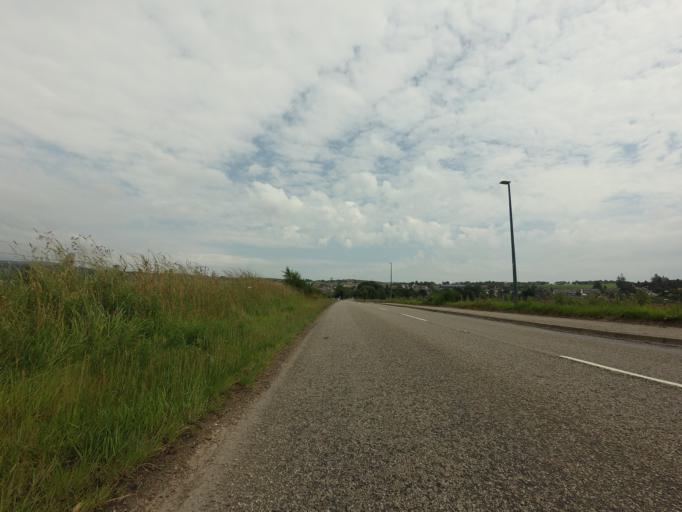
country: GB
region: Scotland
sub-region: Highland
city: Alness
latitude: 57.8895
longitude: -4.3535
